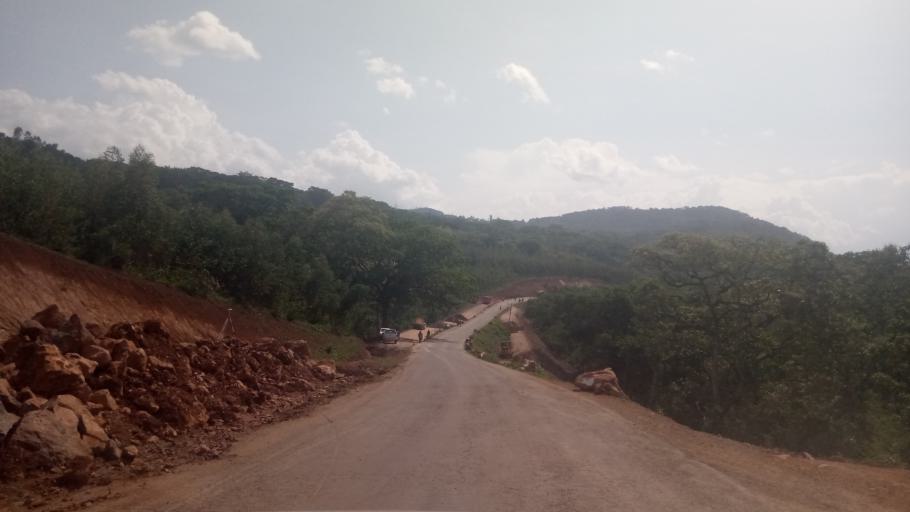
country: ET
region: Oromiya
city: Agaro
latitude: 7.9917
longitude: 36.5089
